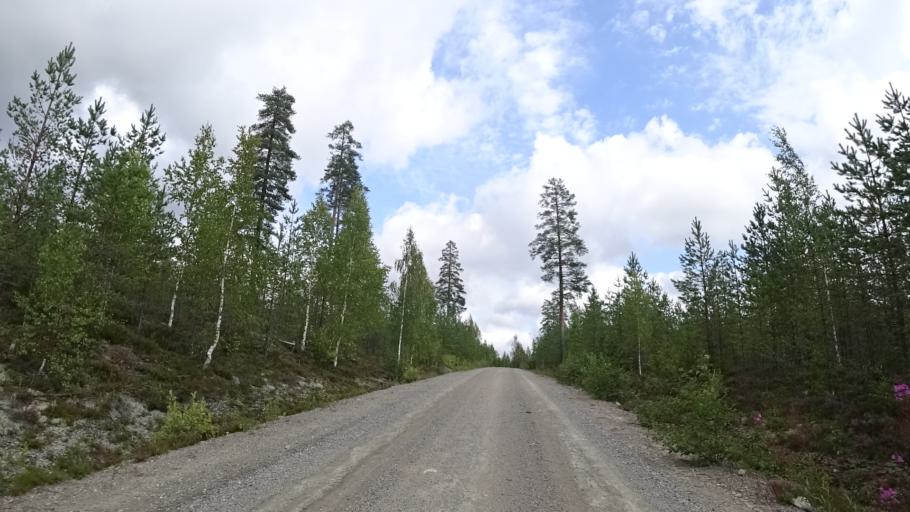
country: FI
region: North Karelia
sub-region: Joensuu
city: Ilomantsi
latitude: 62.9271
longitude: 31.3668
